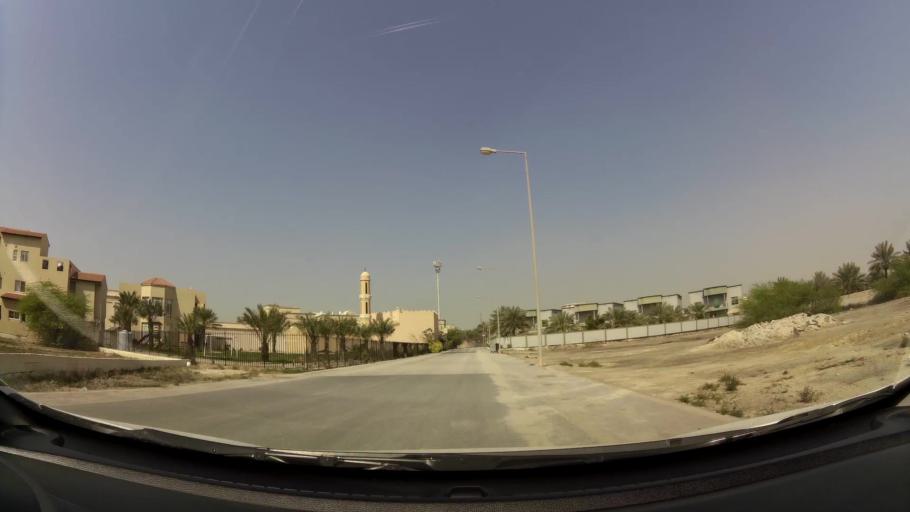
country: BH
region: Northern
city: Madinat `Isa
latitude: 26.1923
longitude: 50.4606
